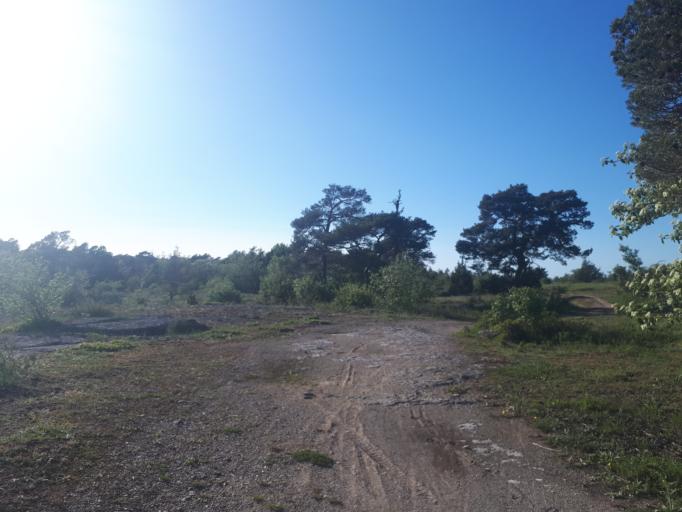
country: SE
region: Gotland
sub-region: Gotland
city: Vibble
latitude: 57.6106
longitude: 18.2528
